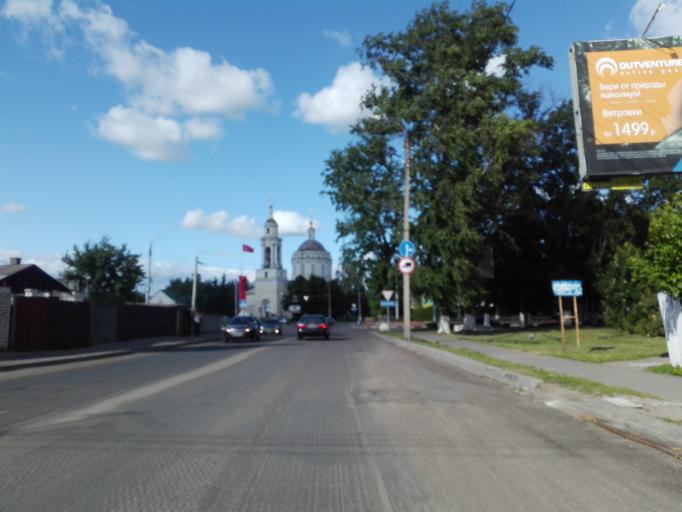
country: RU
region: Orjol
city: Orel
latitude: 52.9605
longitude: 36.0611
